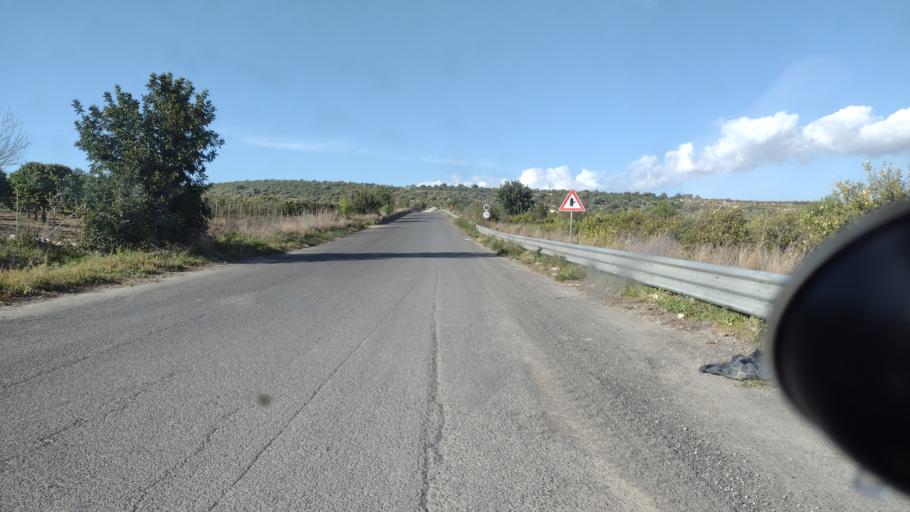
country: IT
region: Sicily
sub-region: Provincia di Siracusa
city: Noto
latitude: 36.8442
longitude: 15.0241
